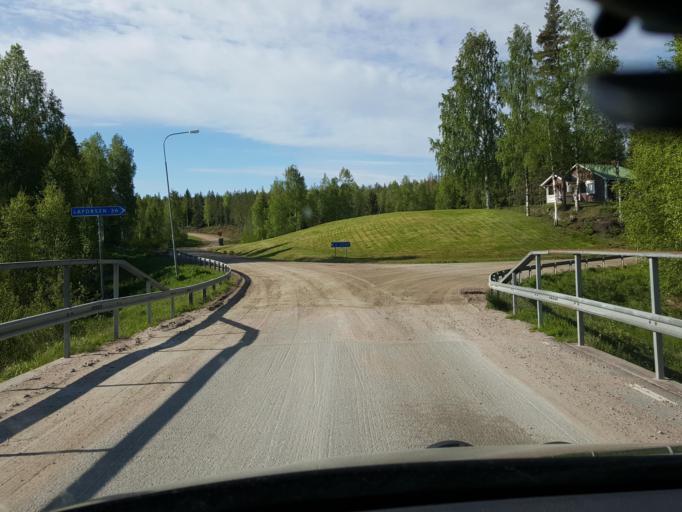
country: SE
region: Vaesternorrland
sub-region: Ange Kommun
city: Ange
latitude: 62.1804
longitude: 15.6321
